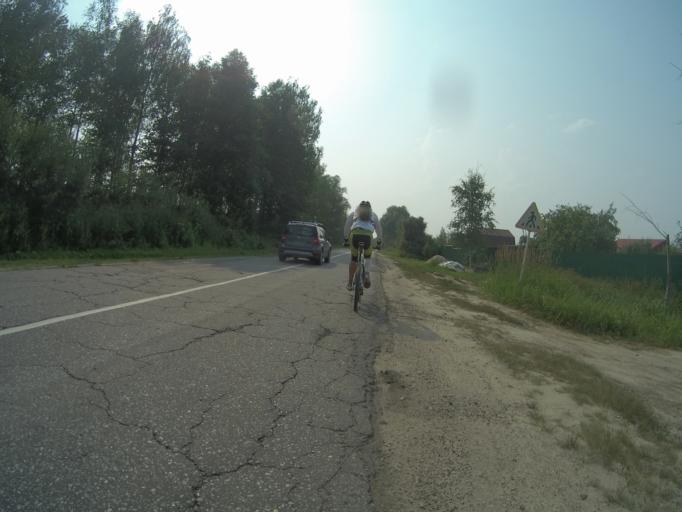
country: RU
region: Vladimir
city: Vorsha
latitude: 56.0109
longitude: 40.1352
